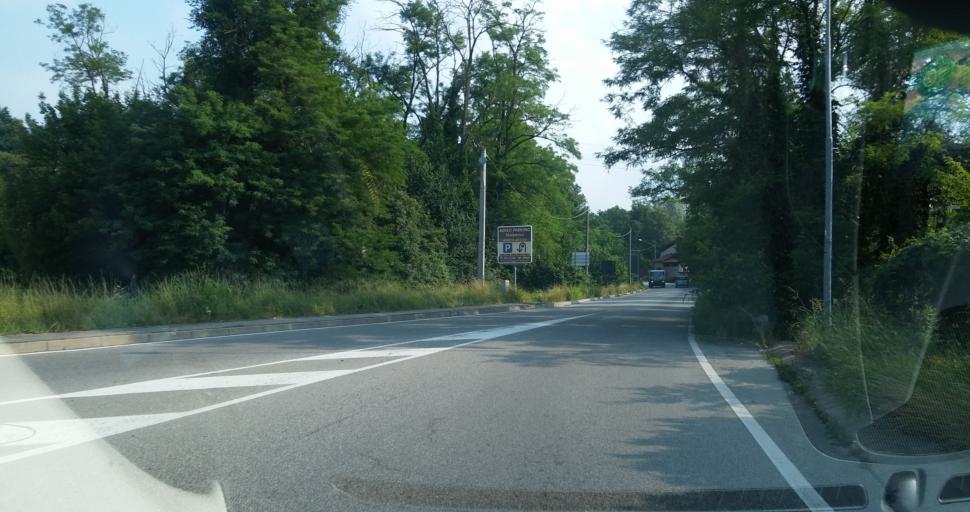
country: IT
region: Lombardy
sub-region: Provincia di Varese
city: Somma Lombardo
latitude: 45.6699
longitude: 8.7054
